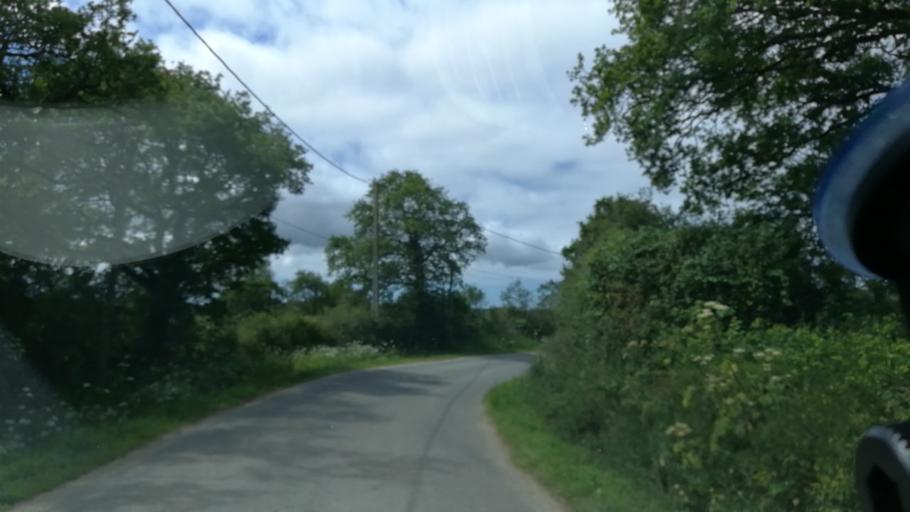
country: FR
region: Pays de la Loire
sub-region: Departement de la Loire-Atlantique
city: Asserac
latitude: 47.4456
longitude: -2.4172
